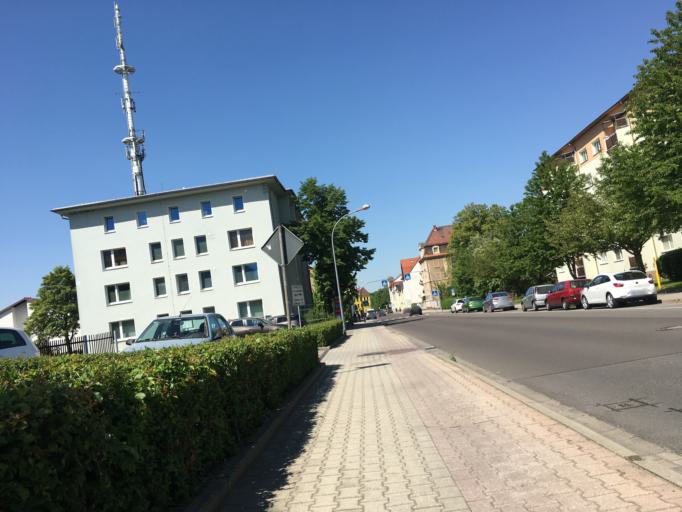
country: DE
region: Saxony
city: Borna
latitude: 51.1191
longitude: 12.4940
